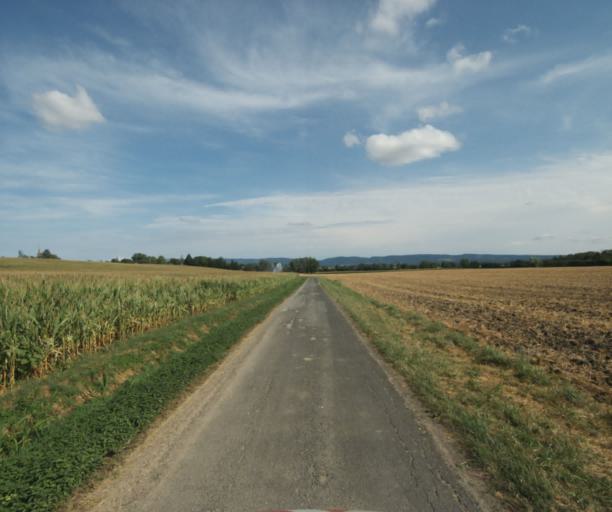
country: FR
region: Midi-Pyrenees
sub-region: Departement du Tarn
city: Puylaurens
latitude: 43.5241
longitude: 1.9779
